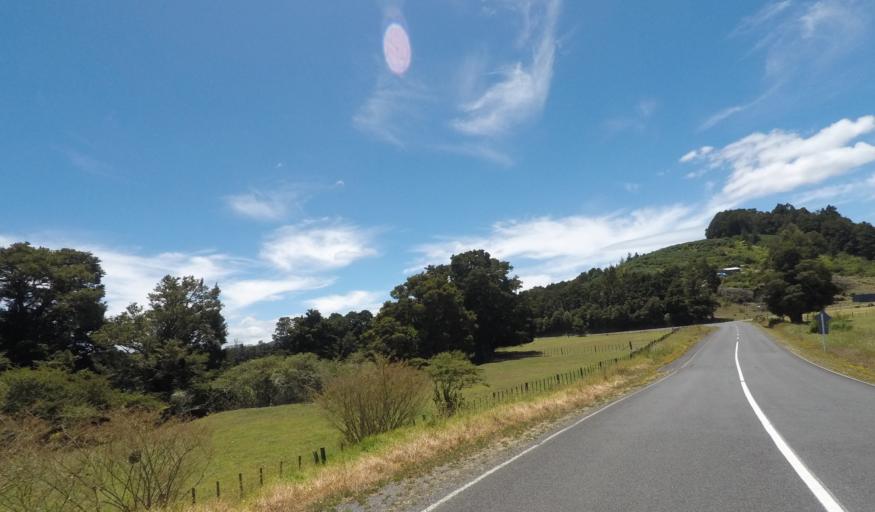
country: NZ
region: Northland
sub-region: Whangarei
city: Whangarei
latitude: -35.5417
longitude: 174.3091
